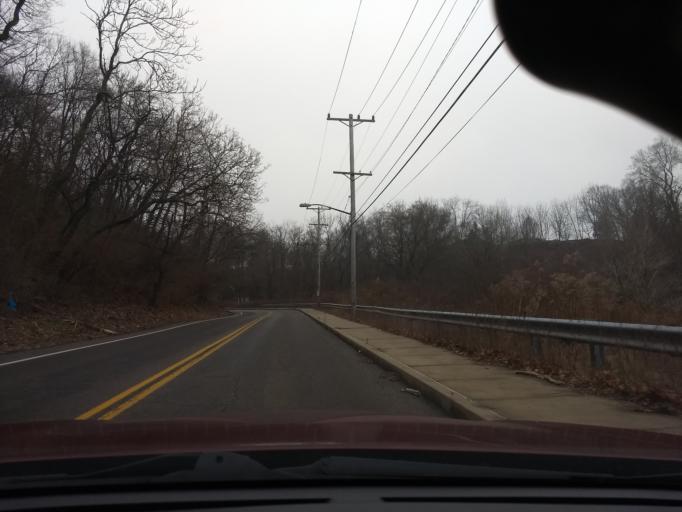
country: US
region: Pennsylvania
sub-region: Allegheny County
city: Homestead
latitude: 40.4238
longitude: -79.9045
